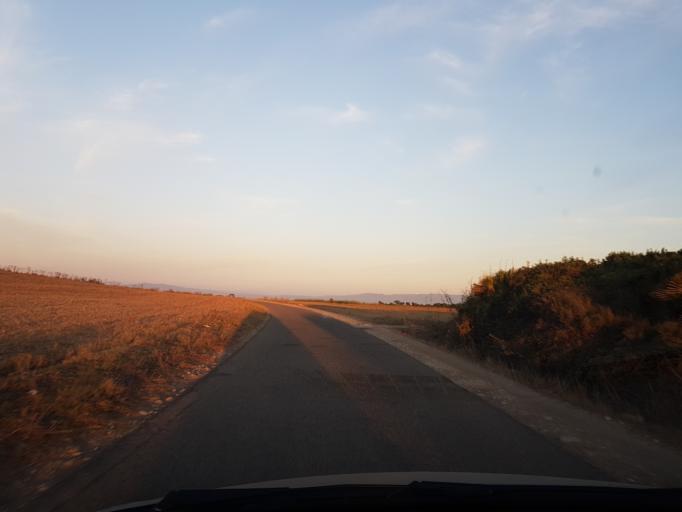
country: IT
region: Sardinia
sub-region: Provincia di Oristano
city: Cabras
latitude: 39.9653
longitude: 8.4337
